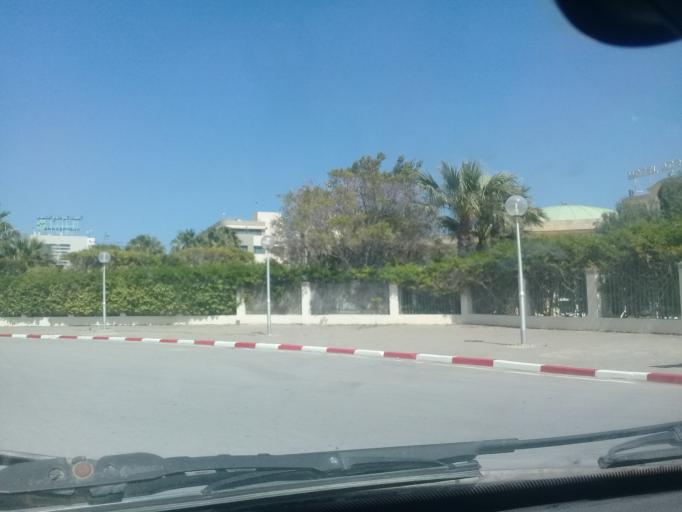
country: TN
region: Ariana
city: Ariana
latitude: 36.8347
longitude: 10.2390
